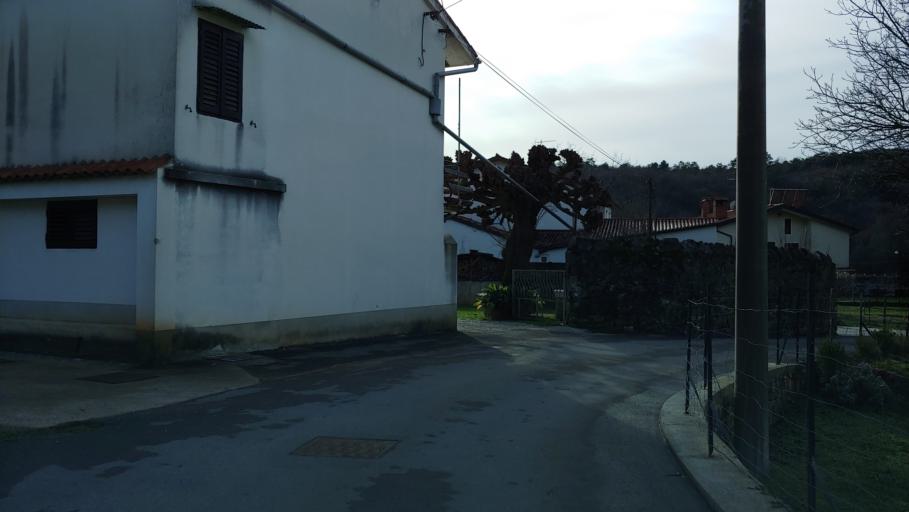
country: IT
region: Friuli Venezia Giulia
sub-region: Provincia di Trieste
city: Sistiana-Visogliano
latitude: 45.8110
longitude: 13.6426
